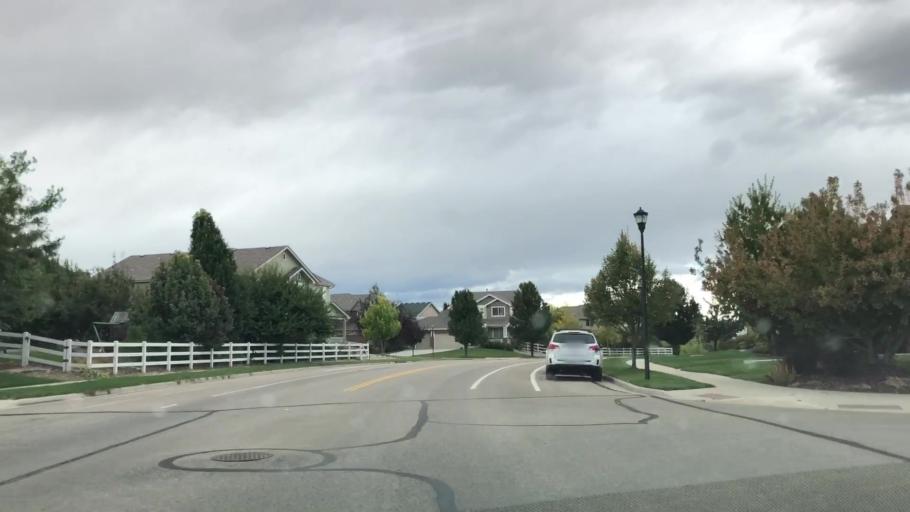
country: US
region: Colorado
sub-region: Larimer County
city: Fort Collins
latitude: 40.5458
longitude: -105.0288
